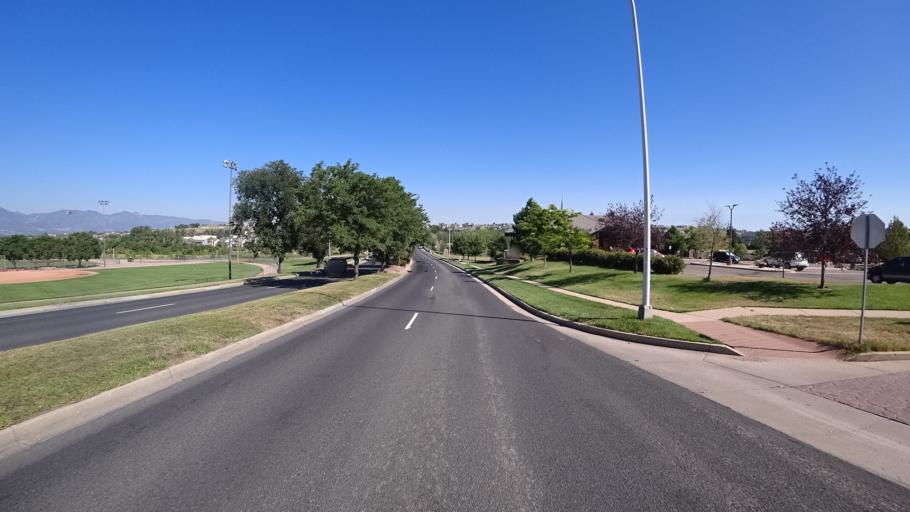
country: US
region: Colorado
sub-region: El Paso County
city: Cimarron Hills
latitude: 38.9285
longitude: -104.7524
